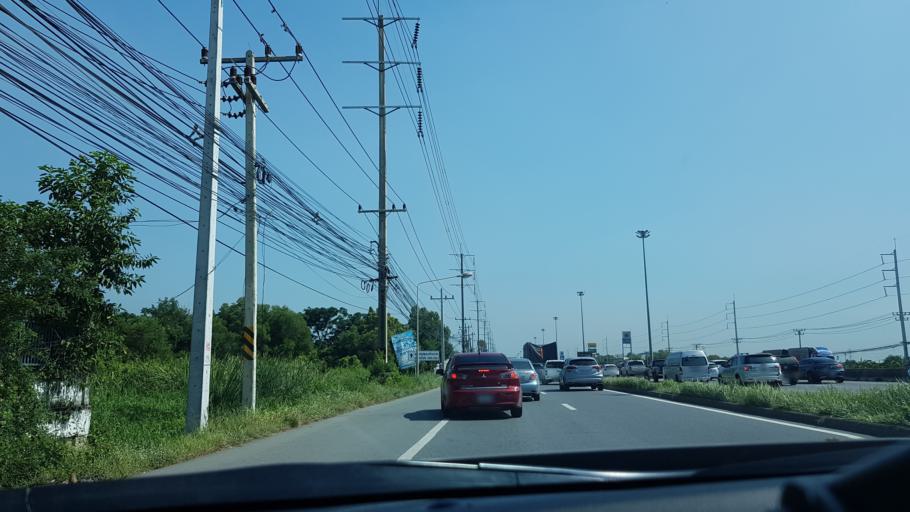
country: TH
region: Sara Buri
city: Nong Khae
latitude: 14.2848
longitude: 100.8152
